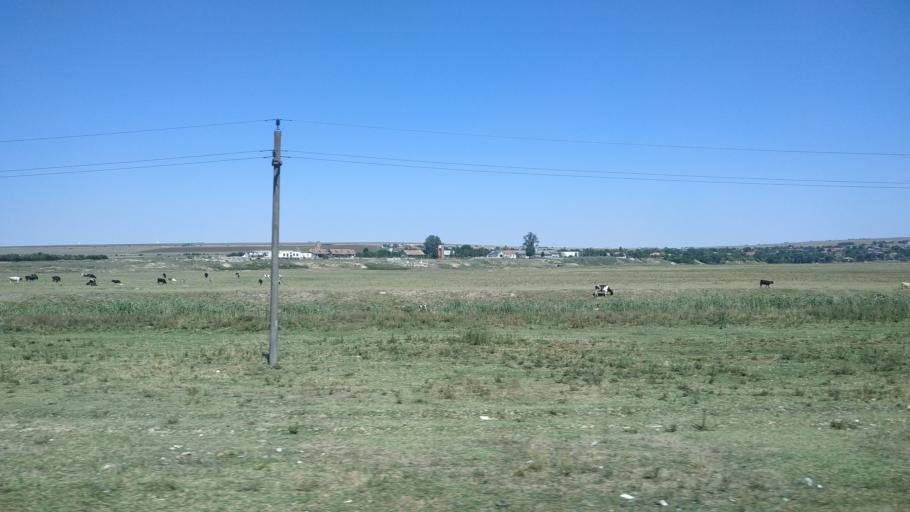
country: RO
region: Constanta
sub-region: Comuna Mircea Voda
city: Satu Nou
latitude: 44.2594
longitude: 28.2157
